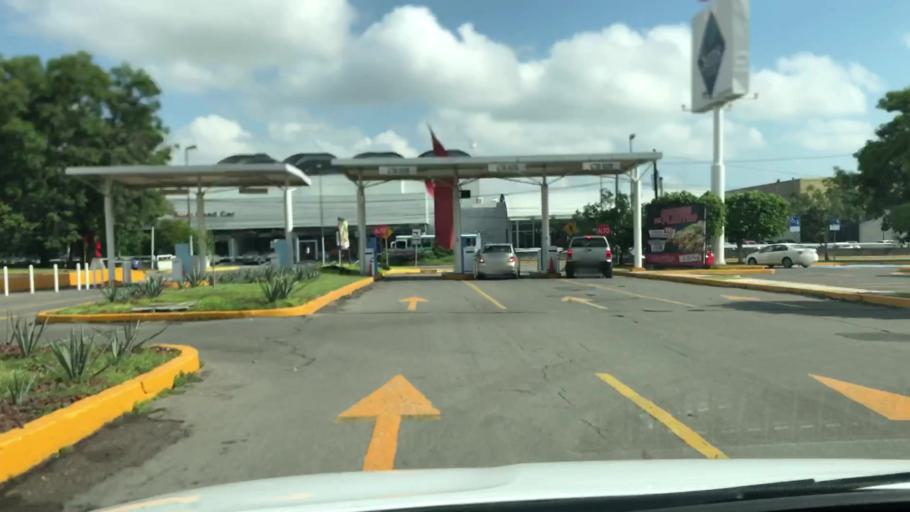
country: MX
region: Jalisco
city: Guadalajara
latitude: 20.6800
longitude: -103.4302
